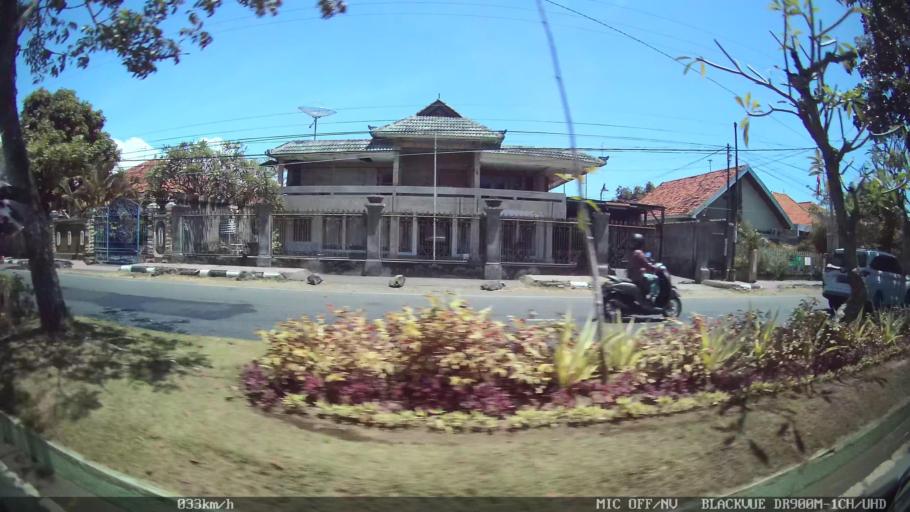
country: ID
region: Bali
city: Banjar Kampunganyar
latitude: -8.1100
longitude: 115.0839
